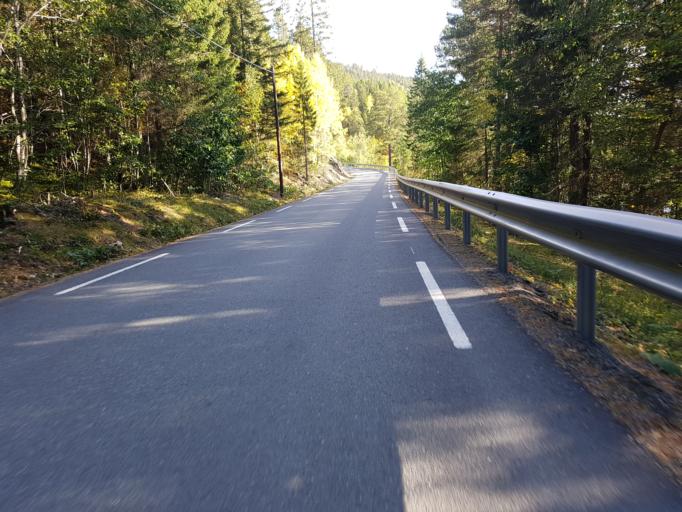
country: NO
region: Sor-Trondelag
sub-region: Malvik
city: Malvik
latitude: 63.3760
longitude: 10.6072
